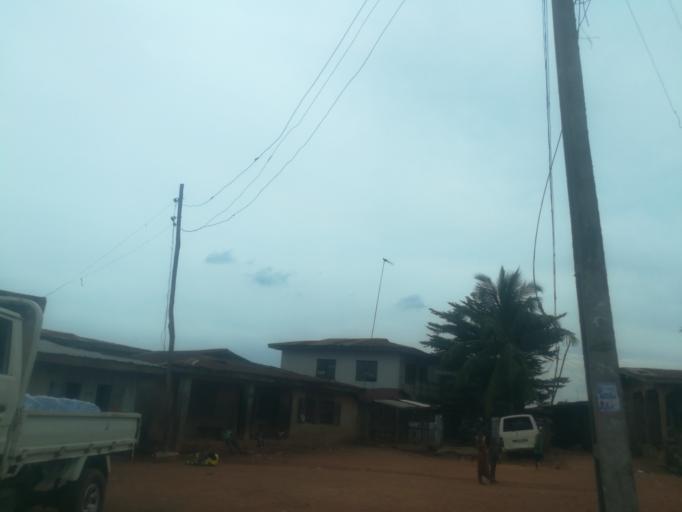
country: NG
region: Oyo
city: Ibadan
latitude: 7.3791
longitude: 3.9328
